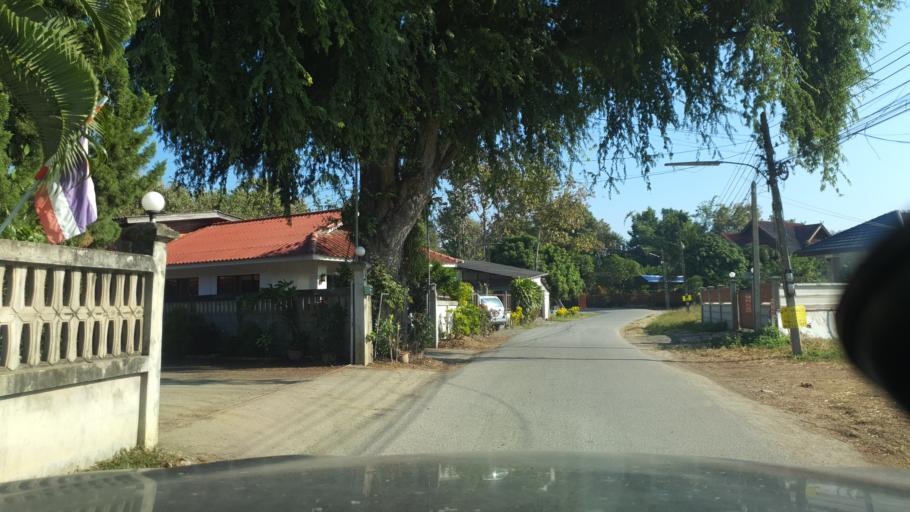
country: TH
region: Chiang Mai
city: San Kamphaeng
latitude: 18.7416
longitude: 99.1714
